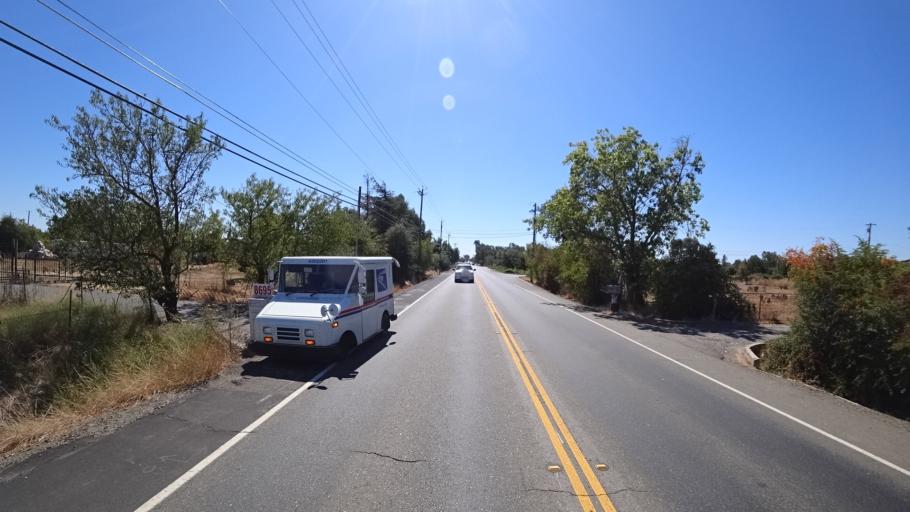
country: US
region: California
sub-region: Sacramento County
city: Vineyard
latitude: 38.4422
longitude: -121.3347
